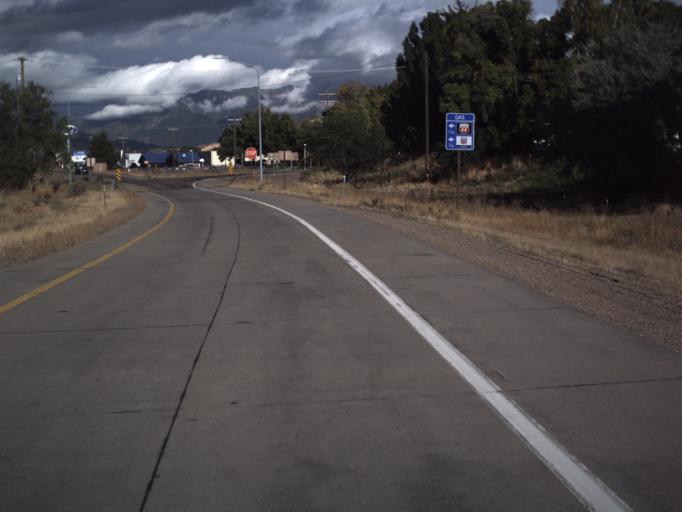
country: US
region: Utah
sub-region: Morgan County
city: Morgan
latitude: 41.0462
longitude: -111.6726
